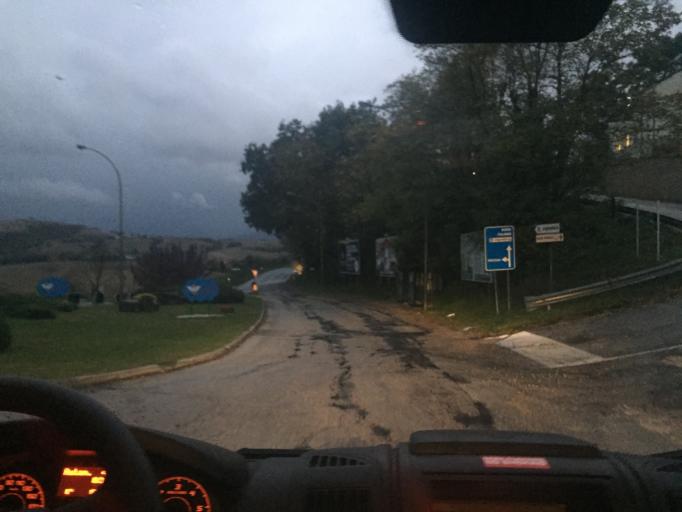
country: IT
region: The Marches
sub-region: Provincia di Macerata
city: Camerino
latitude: 43.1291
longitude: 13.0525
